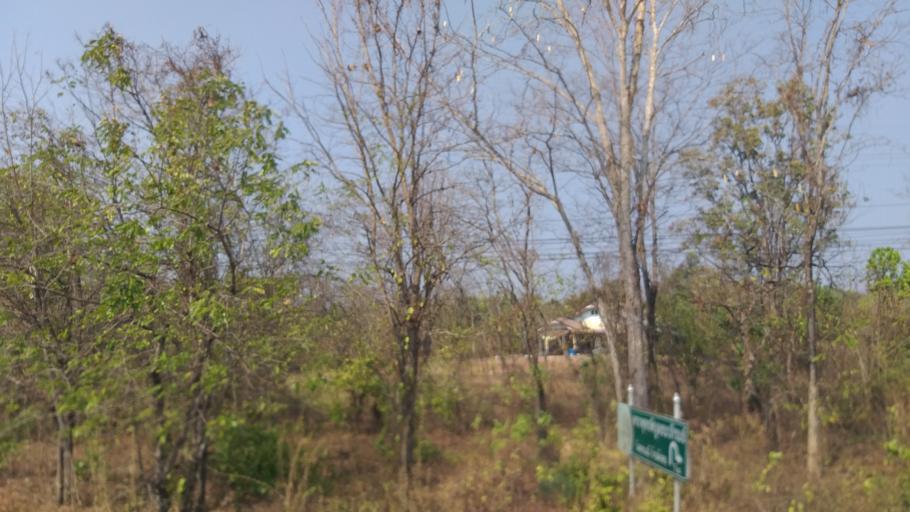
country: TH
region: Changwat Udon Thani
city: Nong Han
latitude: 17.3647
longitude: 103.0329
